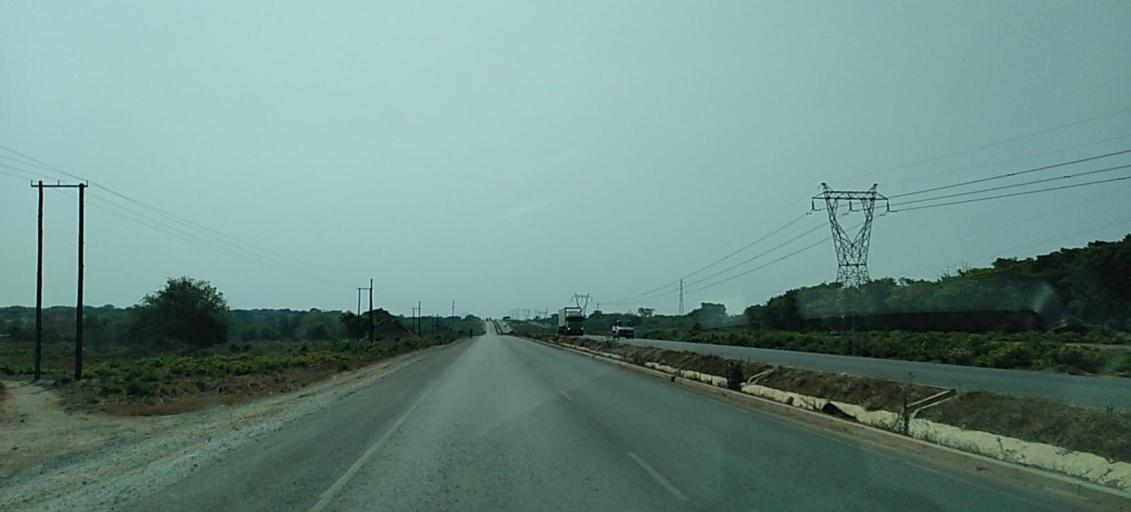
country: ZM
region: Copperbelt
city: Chingola
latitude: -12.5640
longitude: 27.8872
